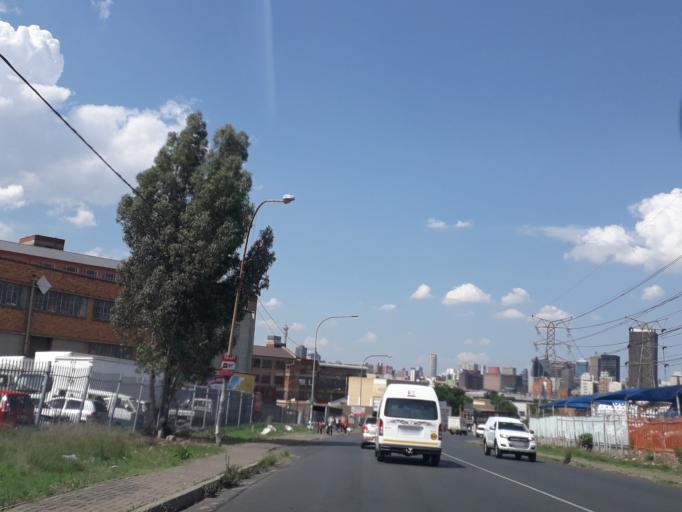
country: ZA
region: Gauteng
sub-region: City of Johannesburg Metropolitan Municipality
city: Johannesburg
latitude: -26.2096
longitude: 28.0219
